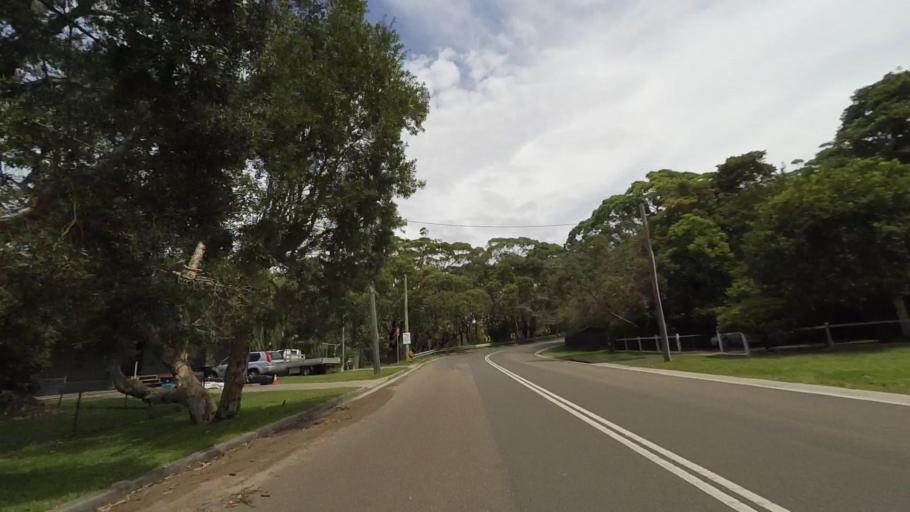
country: AU
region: New South Wales
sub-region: Sutherland Shire
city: Bundeena
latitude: -34.0849
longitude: 151.1437
